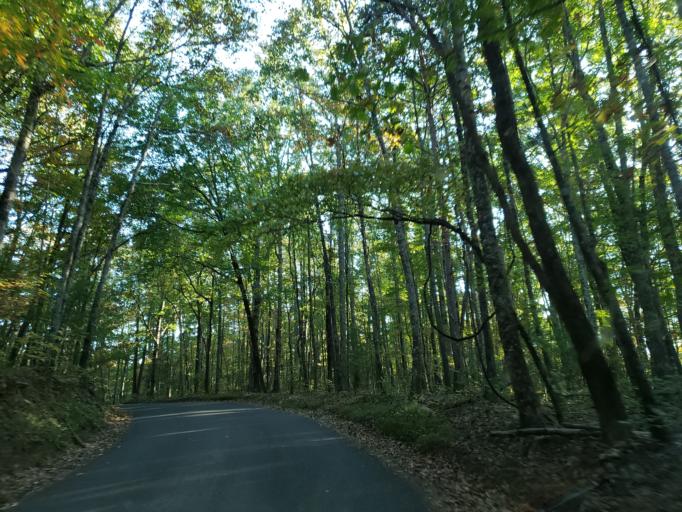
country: US
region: Georgia
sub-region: Gilmer County
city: Ellijay
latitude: 34.6481
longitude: -84.2815
